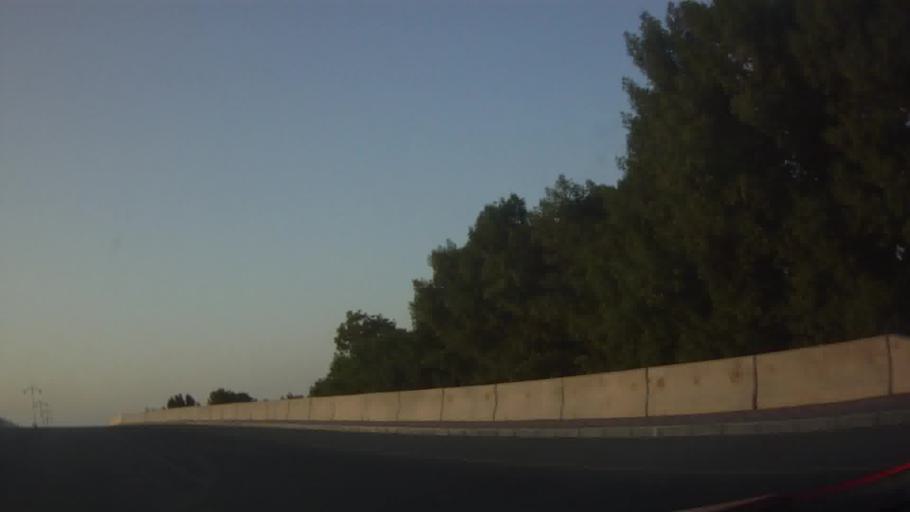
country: OM
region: Muhafazat Masqat
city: Bawshar
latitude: 23.6125
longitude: 58.4736
